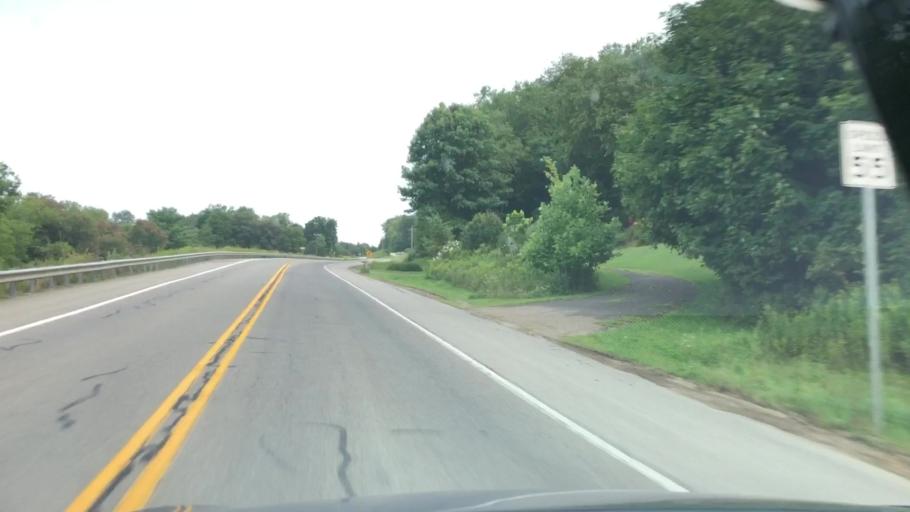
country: US
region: Pennsylvania
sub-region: Venango County
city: Hasson Heights
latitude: 41.5306
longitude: -79.7154
